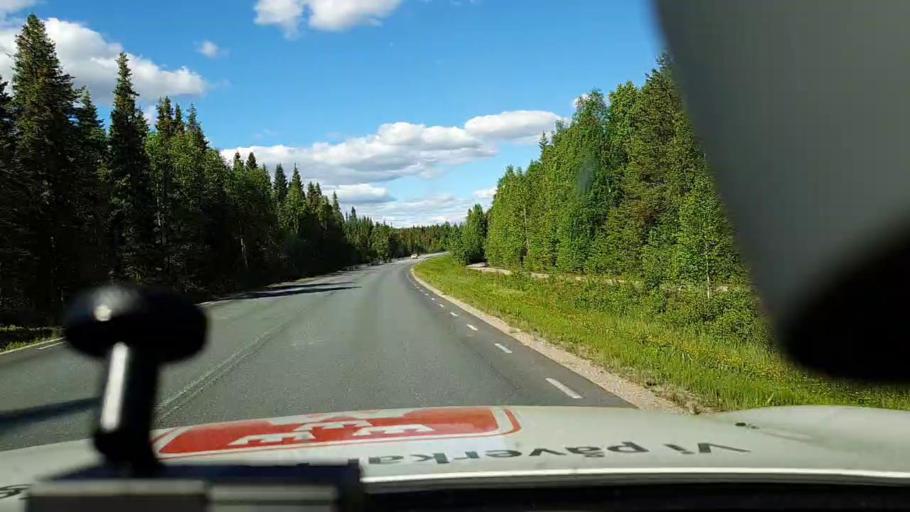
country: FI
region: Lapland
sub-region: Torniolaakso
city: Ylitornio
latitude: 66.3241
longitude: 23.6233
